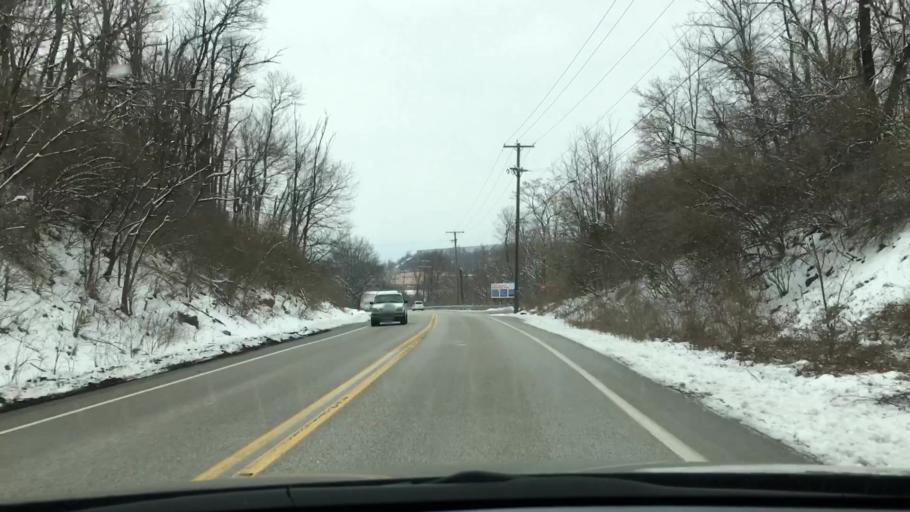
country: US
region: Pennsylvania
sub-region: York County
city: Emigsville
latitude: 40.0156
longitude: -76.7188
